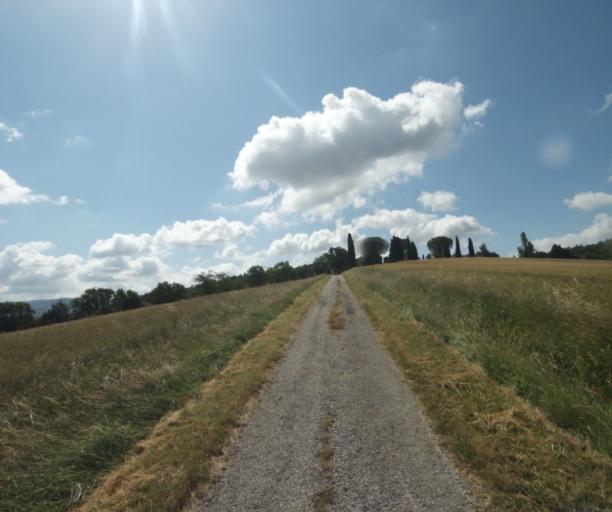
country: FR
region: Midi-Pyrenees
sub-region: Departement de la Haute-Garonne
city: Saint-Felix-Lauragais
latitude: 43.4270
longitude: 1.9310
